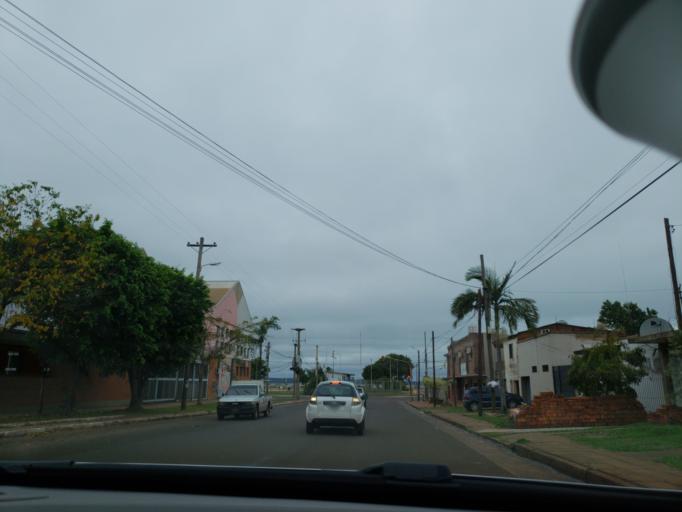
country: AR
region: Misiones
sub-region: Departamento de Capital
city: Posadas
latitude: -27.3950
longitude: -55.8949
